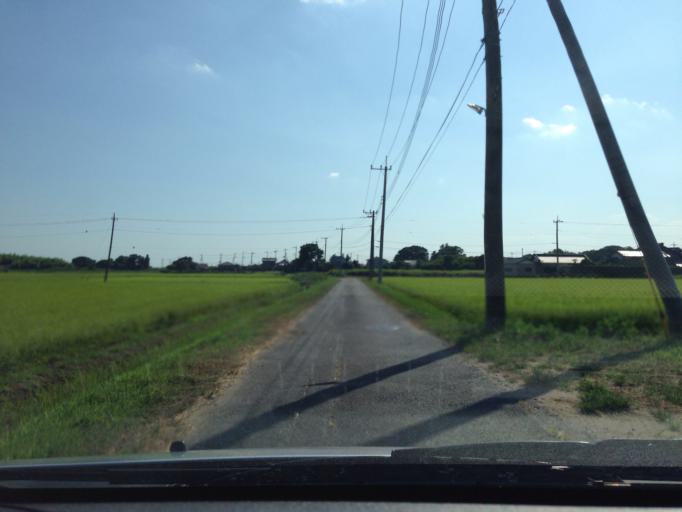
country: JP
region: Ibaraki
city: Inashiki
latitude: 36.0012
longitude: 140.3676
